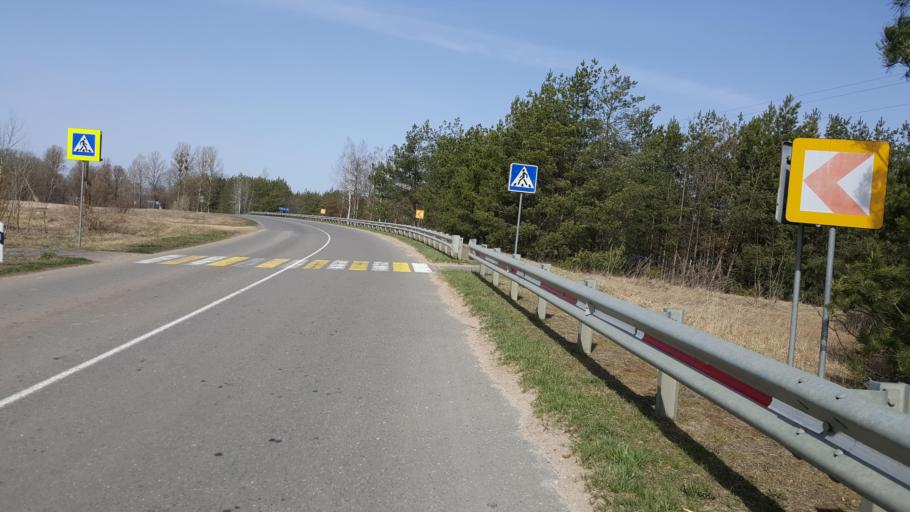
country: BY
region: Brest
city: Kamyanyuki
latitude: 52.4896
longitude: 23.6907
